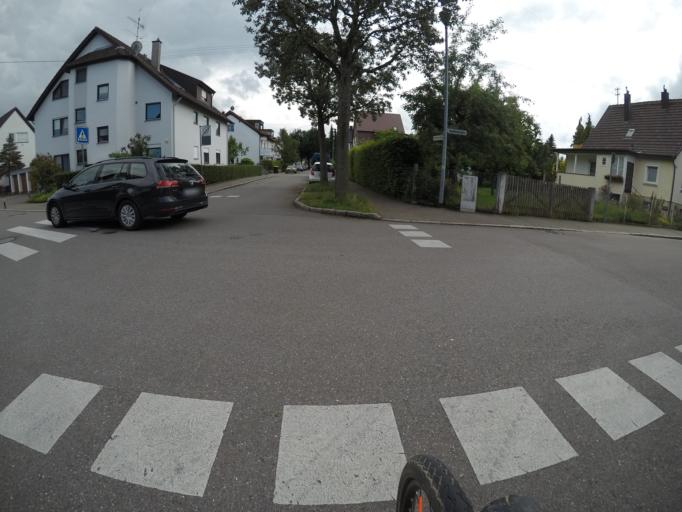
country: DE
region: Baden-Wuerttemberg
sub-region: Regierungsbezirk Stuttgart
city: Leinfelden-Echterdingen
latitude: 48.6866
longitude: 9.1702
